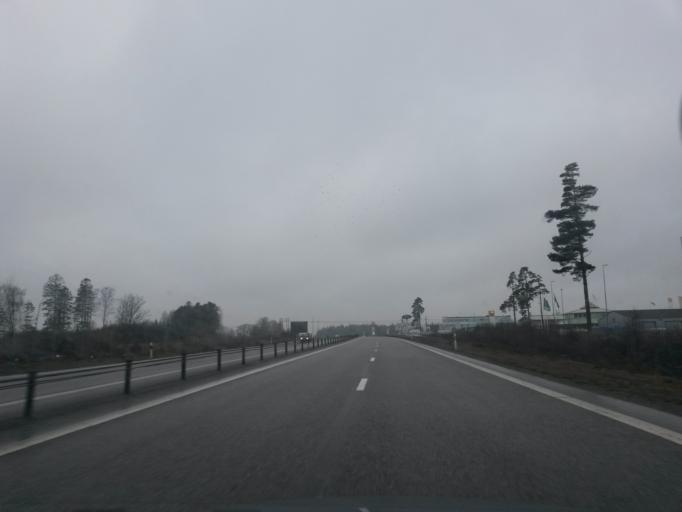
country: SE
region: Vaestra Goetaland
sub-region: Trollhattan
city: Trollhattan
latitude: 58.3387
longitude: 12.2501
